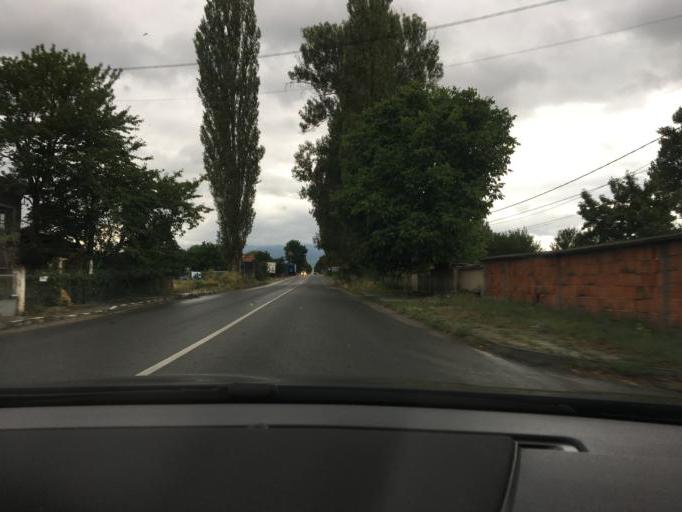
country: BG
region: Kyustendil
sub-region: Obshtina Kyustendil
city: Kyustendil
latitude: 42.2804
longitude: 22.7279
